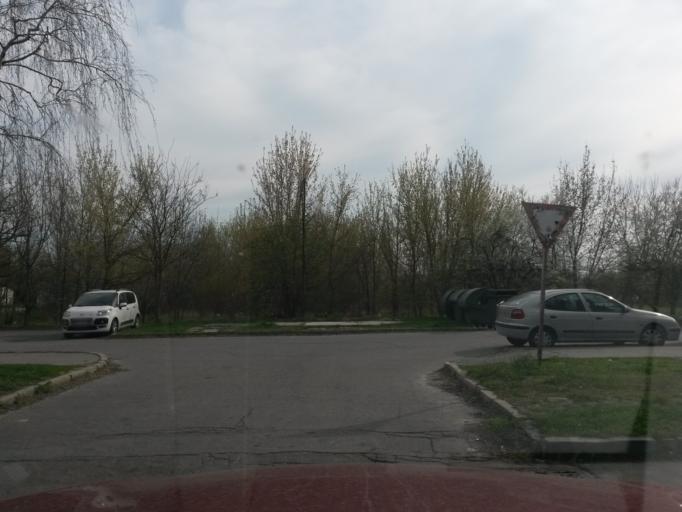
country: SK
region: Nitriansky
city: Komarno
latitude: 47.7702
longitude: 18.1218
